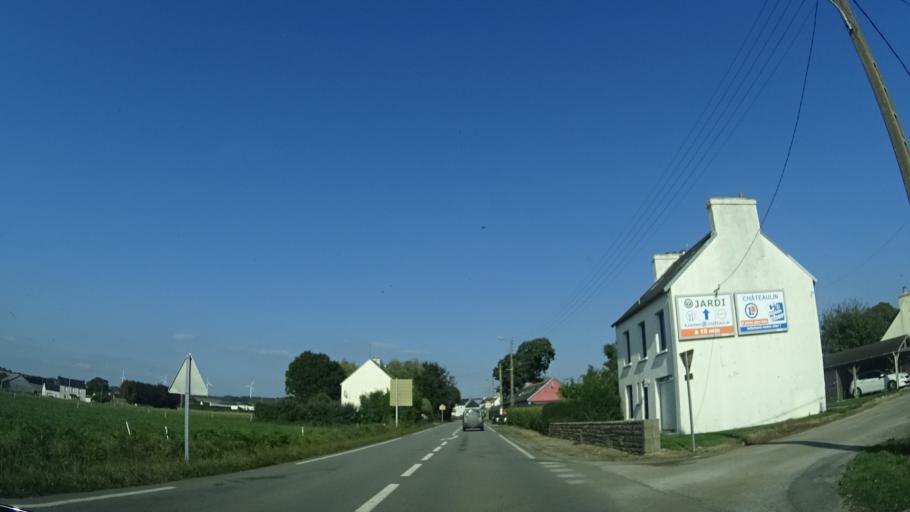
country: FR
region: Brittany
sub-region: Departement du Finistere
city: Cast
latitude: 48.1508
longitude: -4.1442
